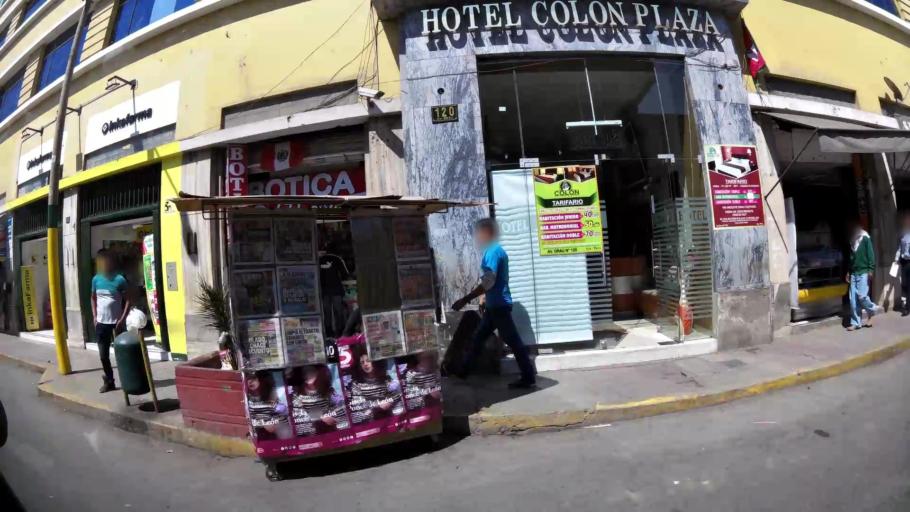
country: PE
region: Ica
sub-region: Provincia de Ica
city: Ica
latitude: -14.0633
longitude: -75.7285
